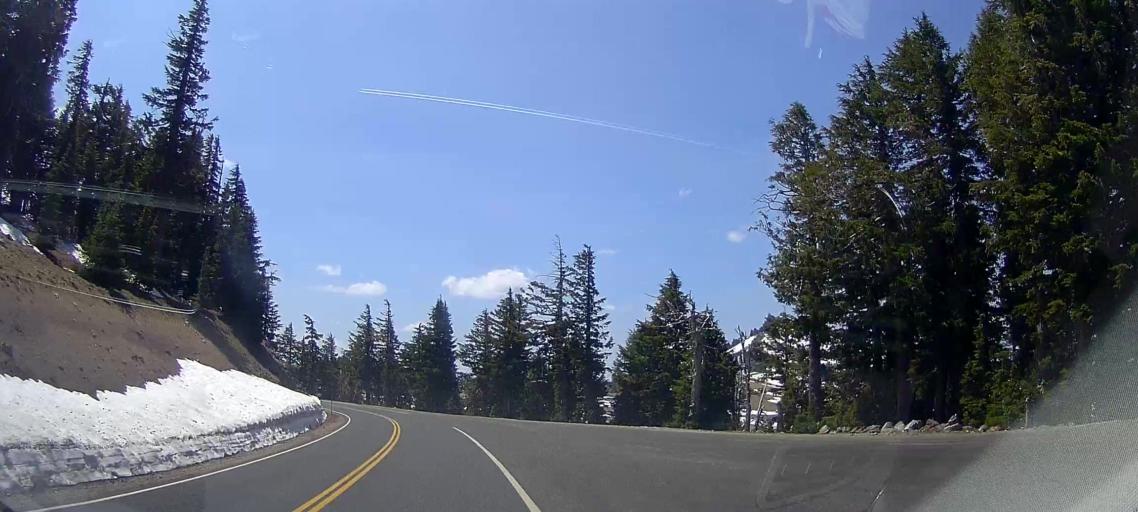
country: US
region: Oregon
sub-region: Jackson County
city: Shady Cove
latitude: 42.9697
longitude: -122.1499
